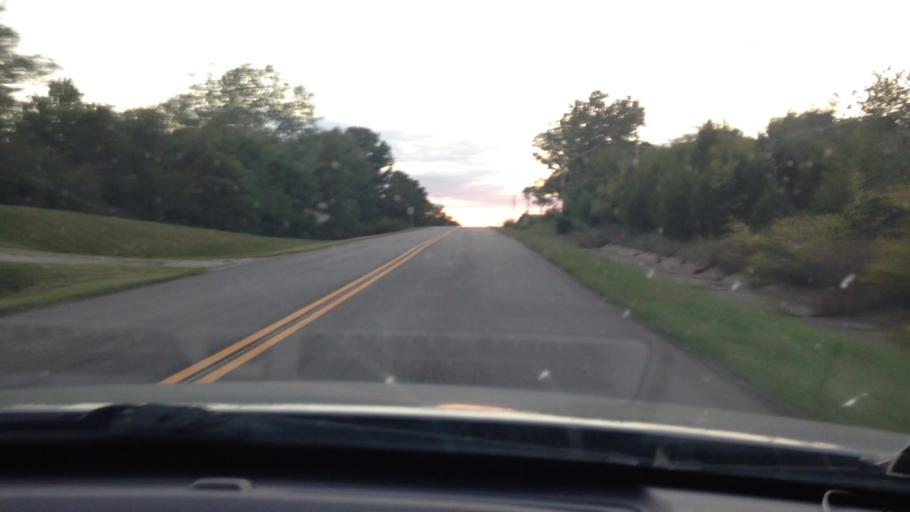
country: US
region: Kansas
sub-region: Leavenworth County
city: Lansing
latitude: 39.1868
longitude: -94.8893
